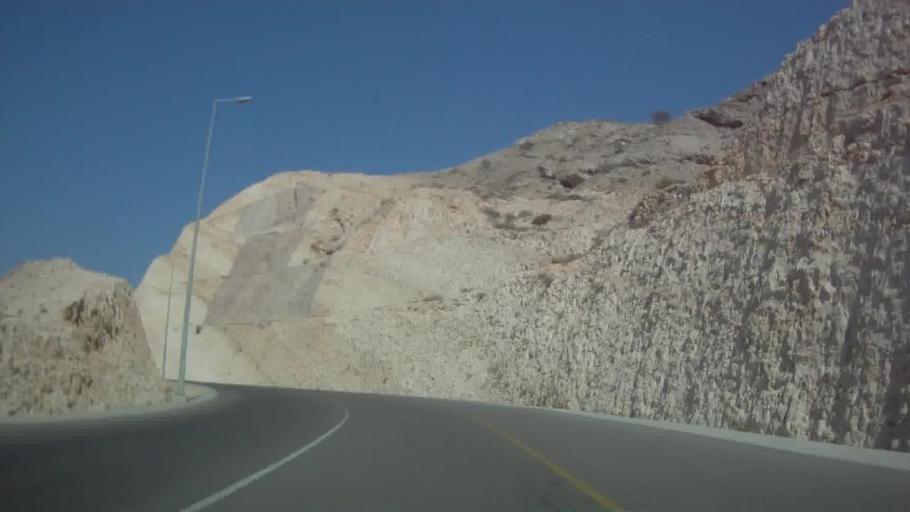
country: OM
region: Muhafazat Masqat
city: Muscat
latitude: 23.5431
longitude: 58.6508
